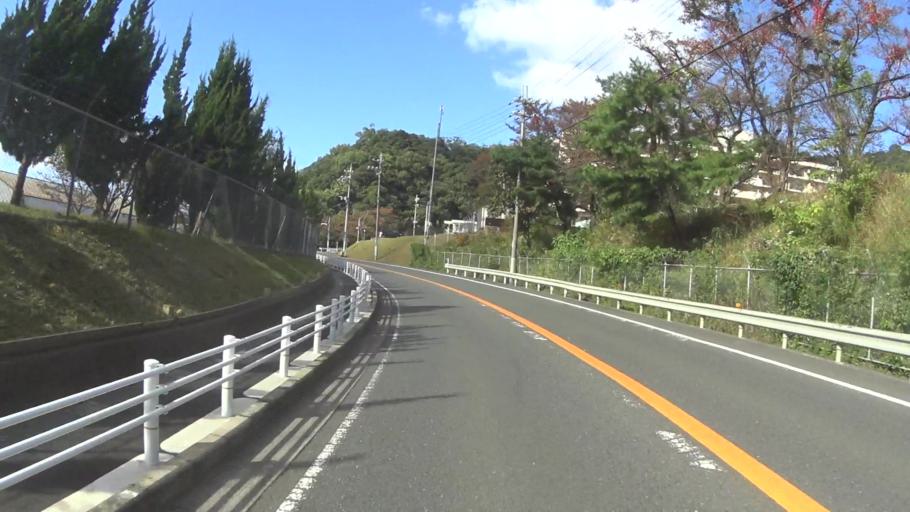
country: JP
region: Kyoto
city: Maizuru
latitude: 35.4805
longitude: 135.4002
